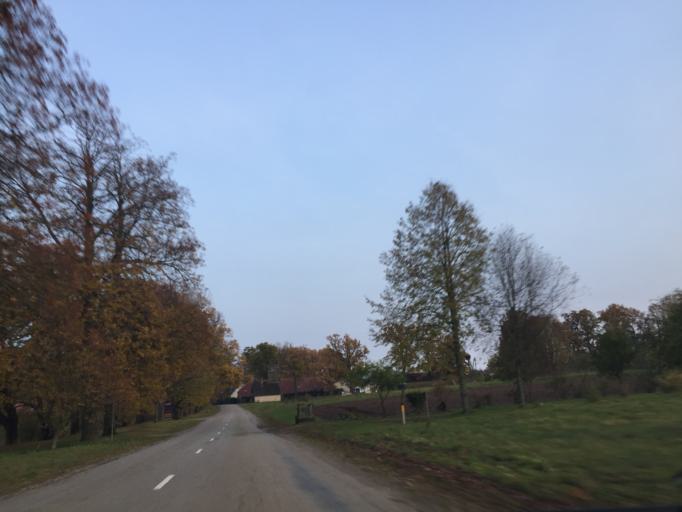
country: LV
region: Cesu Rajons
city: Cesis
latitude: 57.3139
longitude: 25.1532
